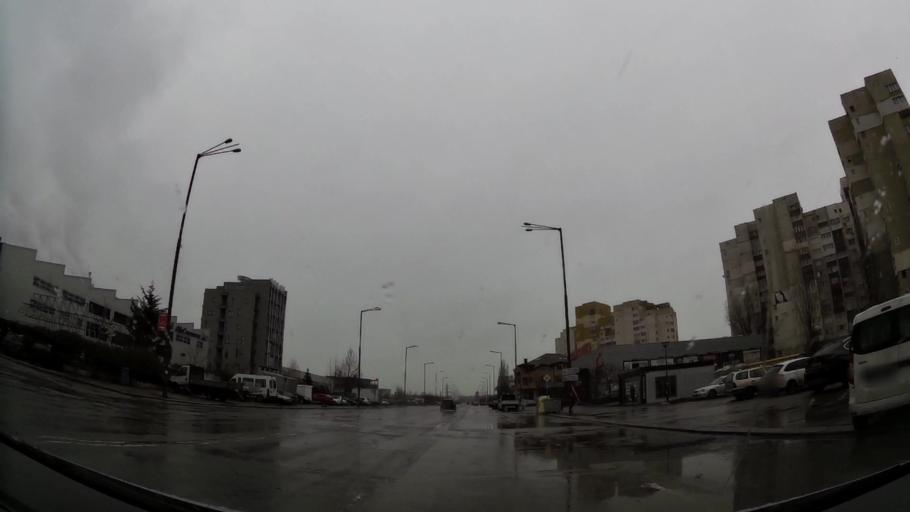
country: BG
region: Sofia-Capital
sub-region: Stolichna Obshtina
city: Sofia
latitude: 42.6505
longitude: 23.4069
